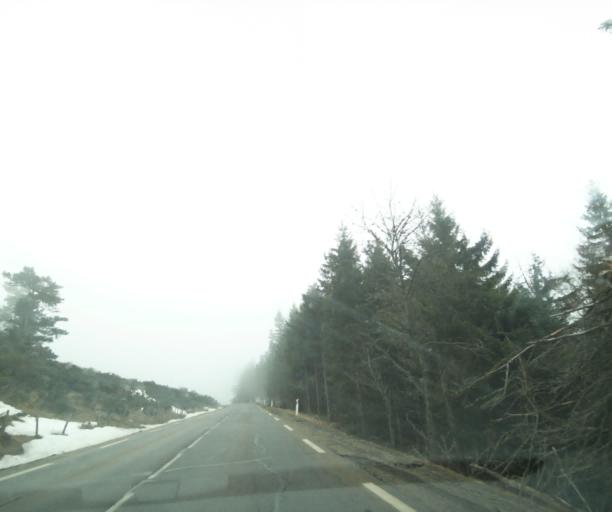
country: FR
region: Languedoc-Roussillon
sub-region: Departement de la Lozere
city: Langogne
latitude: 44.7023
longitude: 4.0157
